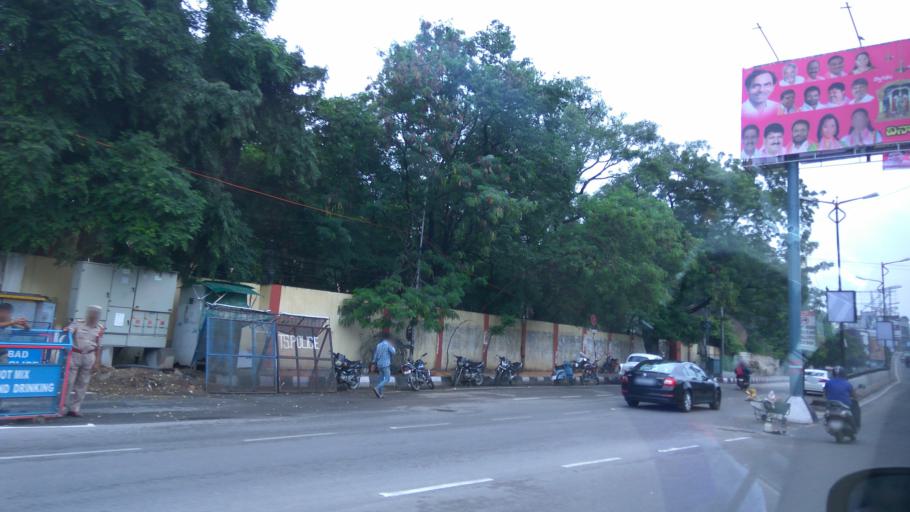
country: IN
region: Telangana
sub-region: Hyderabad
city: Hyderabad
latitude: 17.4322
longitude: 78.4562
